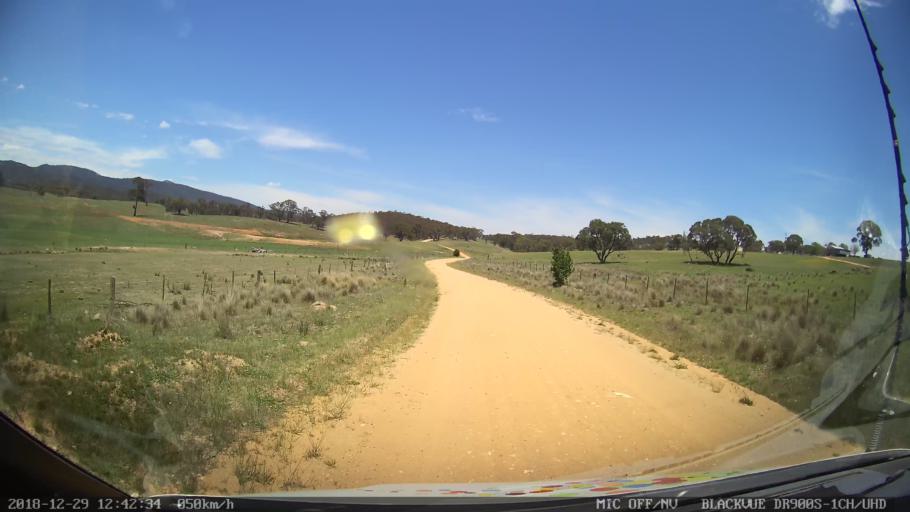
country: AU
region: Australian Capital Territory
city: Macarthur
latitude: -35.6137
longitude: 149.2190
